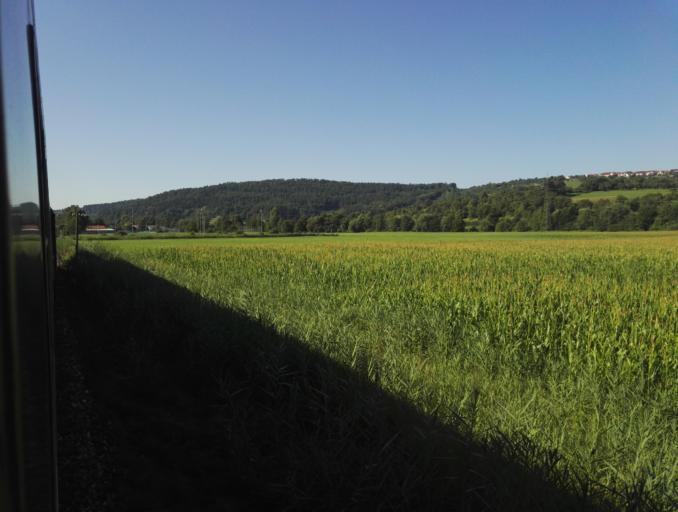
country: DE
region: Baden-Wuerttemberg
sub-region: Regierungsbezirk Stuttgart
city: Rudersberg
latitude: 48.8514
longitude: 9.5379
